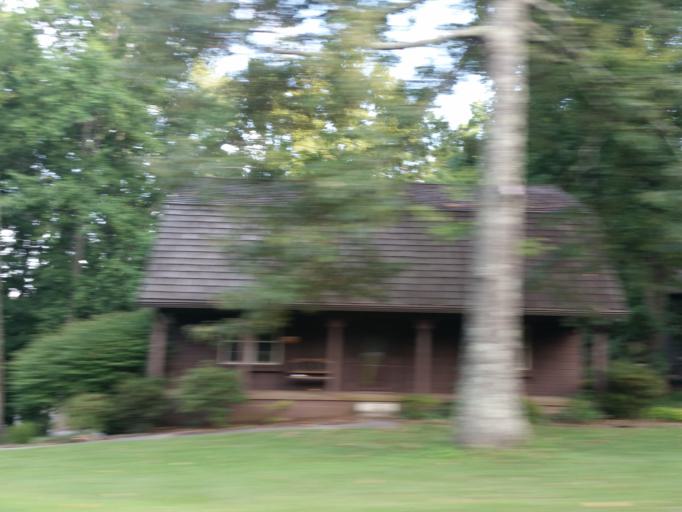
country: US
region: Tennessee
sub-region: Knox County
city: Knoxville
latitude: 36.0434
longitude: -83.9461
